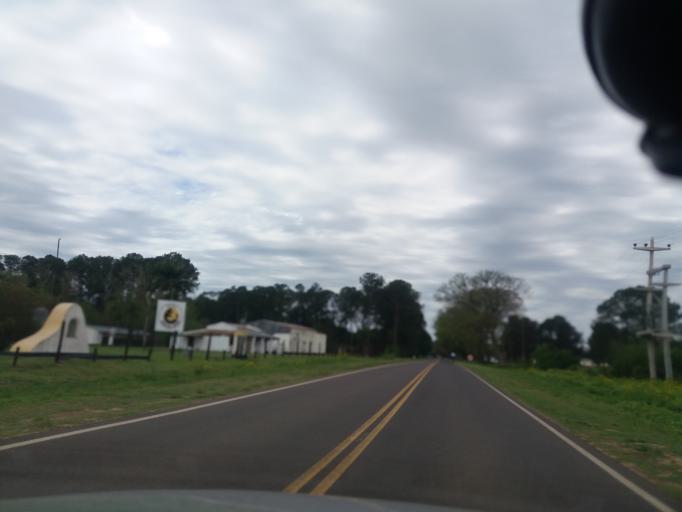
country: AR
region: Corrientes
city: Riachuelo
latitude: -27.4565
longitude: -58.6935
